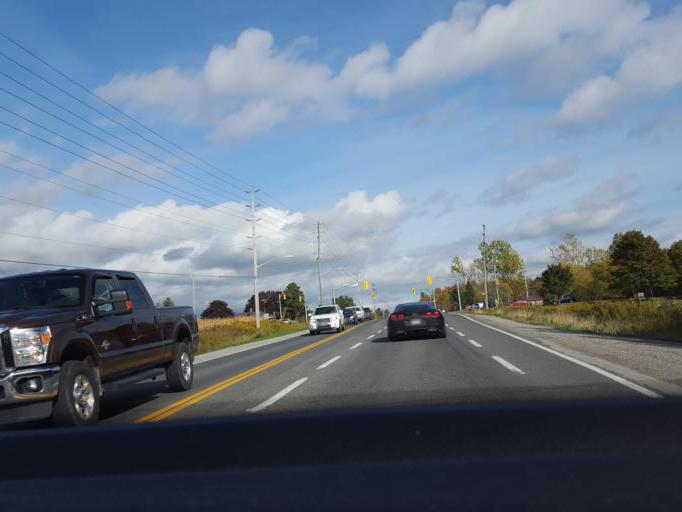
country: CA
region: Ontario
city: Oshawa
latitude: 43.9720
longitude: -78.7098
